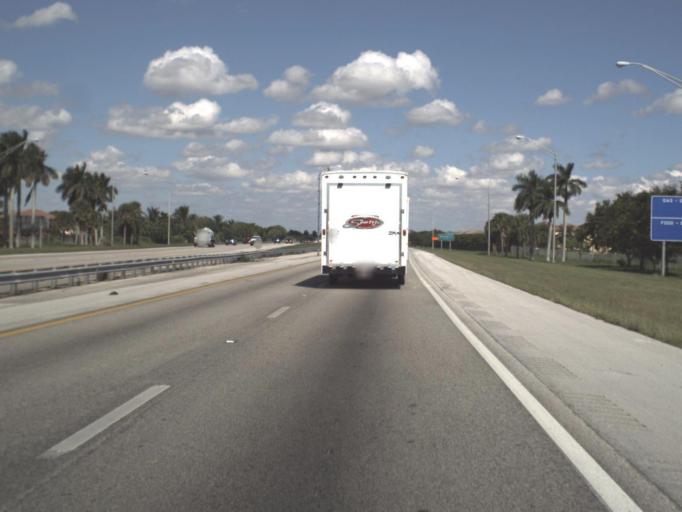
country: US
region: Florida
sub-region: Miami-Dade County
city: Goulds
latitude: 25.5497
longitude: -80.3627
